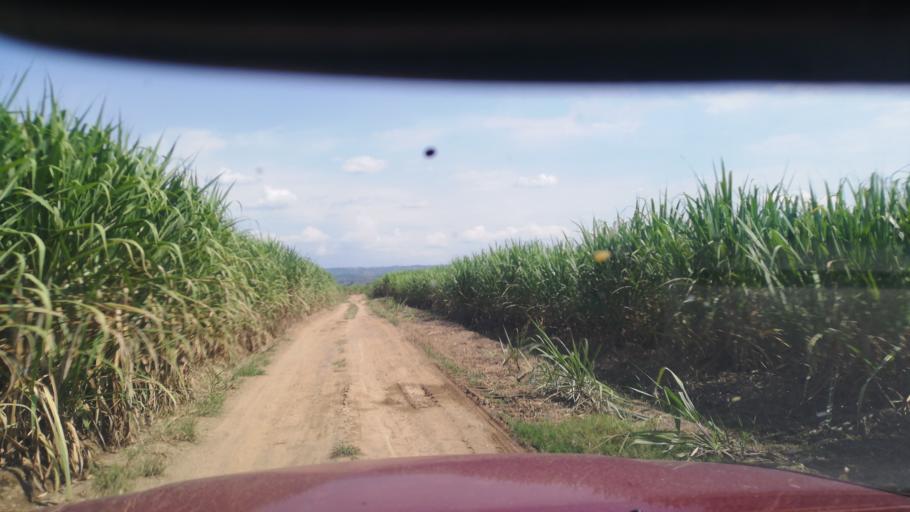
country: CO
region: Risaralda
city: La Virginia
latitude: 4.8985
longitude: -75.9293
